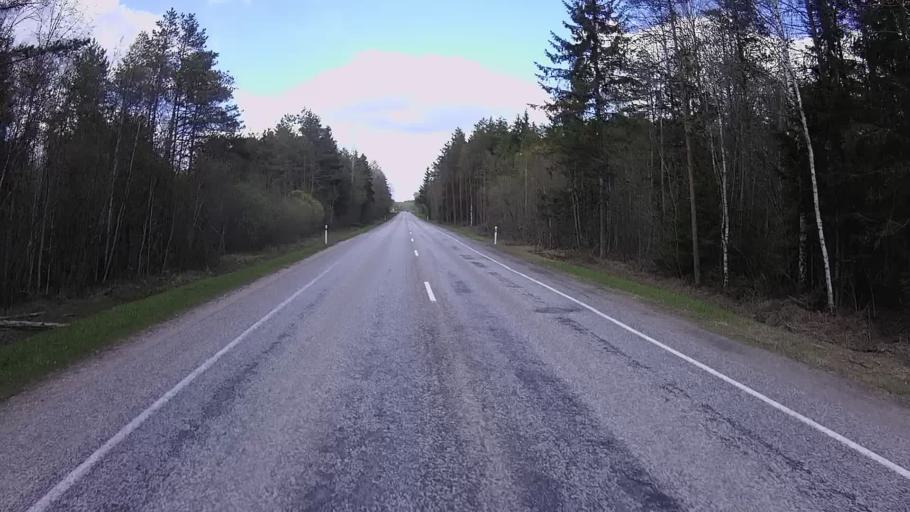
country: EE
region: Jogevamaa
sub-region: Jogeva linn
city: Jogeva
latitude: 58.7663
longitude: 26.4411
